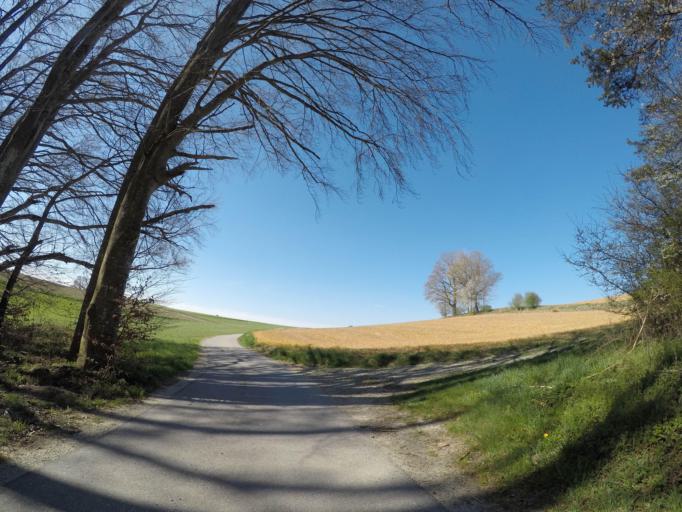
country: DE
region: Baden-Wuerttemberg
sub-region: Tuebingen Region
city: Guggenhausen
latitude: 47.8764
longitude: 9.4547
